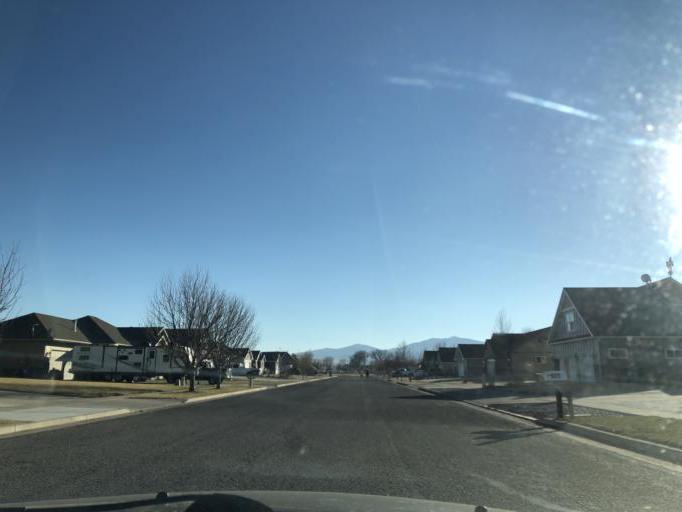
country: US
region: Utah
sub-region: Cache County
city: Wellsville
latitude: 41.6521
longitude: -111.9114
